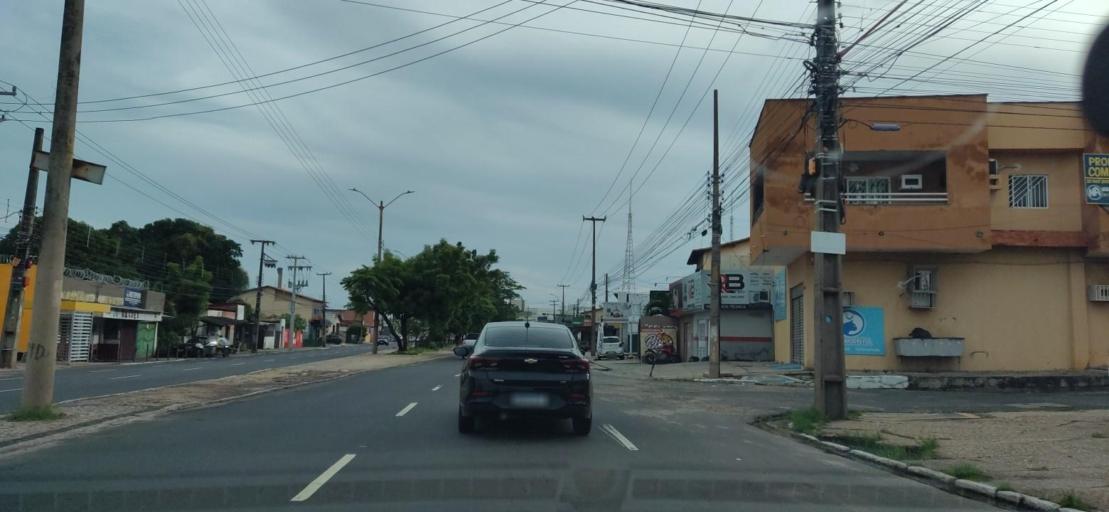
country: BR
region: Piaui
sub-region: Teresina
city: Teresina
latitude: -5.1078
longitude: -42.7926
